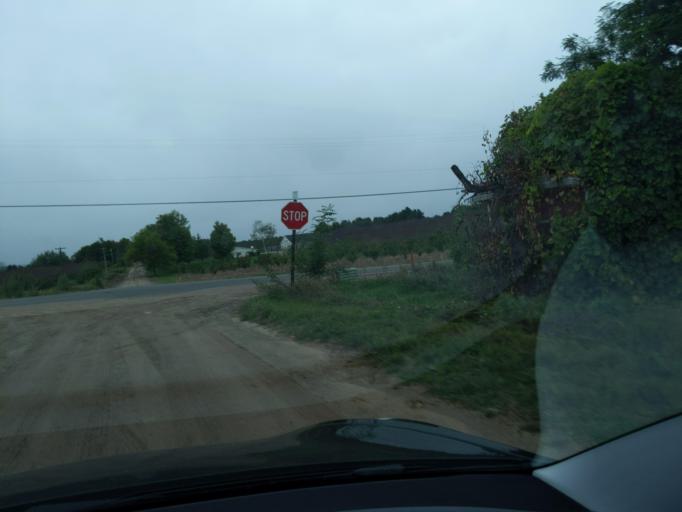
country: US
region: Michigan
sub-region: Antrim County
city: Elk Rapids
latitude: 44.8165
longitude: -85.4044
